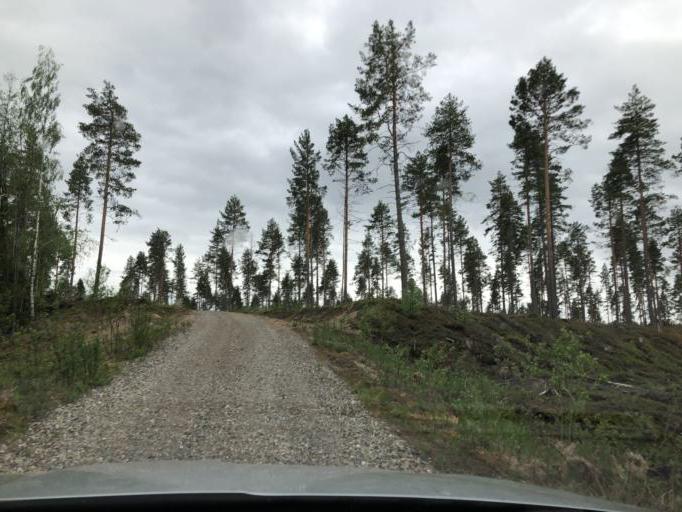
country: SE
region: Norrbotten
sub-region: Pitea Kommun
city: Roknas
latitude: 65.3998
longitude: 21.2687
